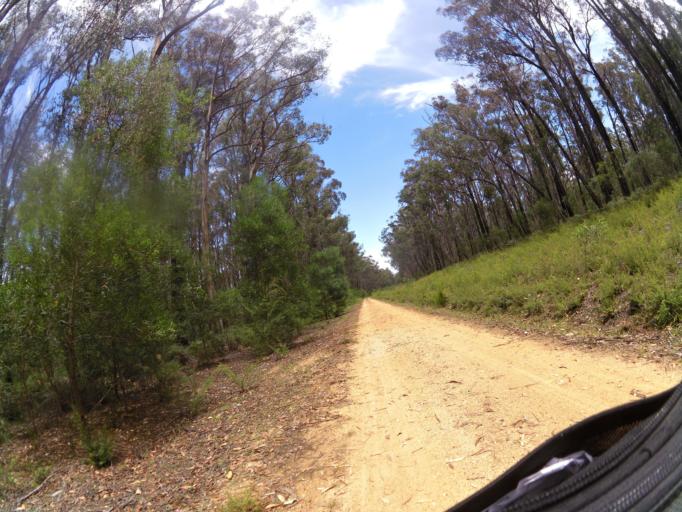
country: AU
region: Victoria
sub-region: East Gippsland
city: Lakes Entrance
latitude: -37.7419
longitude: 148.0027
